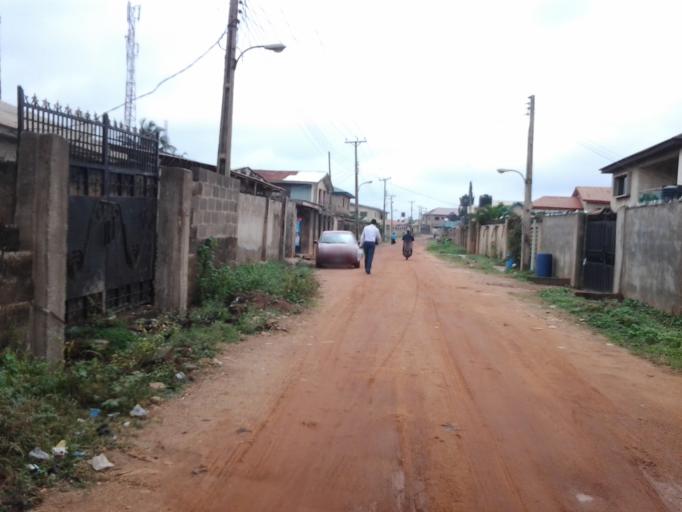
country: NG
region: Oyo
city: Ibadan
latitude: 7.4293
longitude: 3.9551
